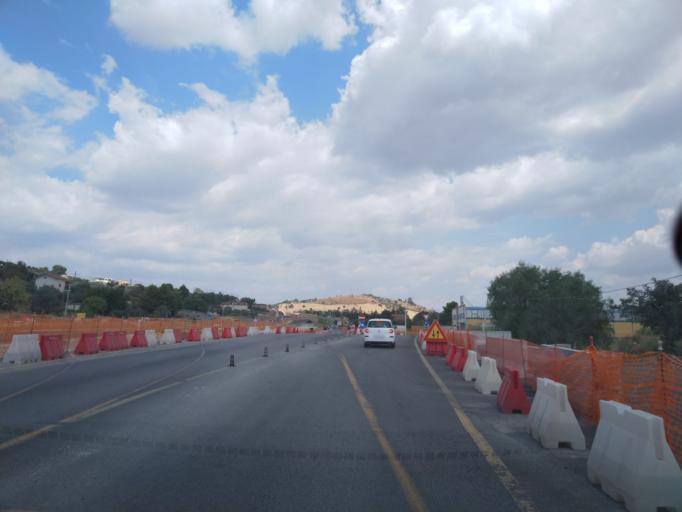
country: IT
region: Sicily
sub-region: Provincia di Caltanissetta
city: San Cataldo
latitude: 37.4540
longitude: 13.9830
